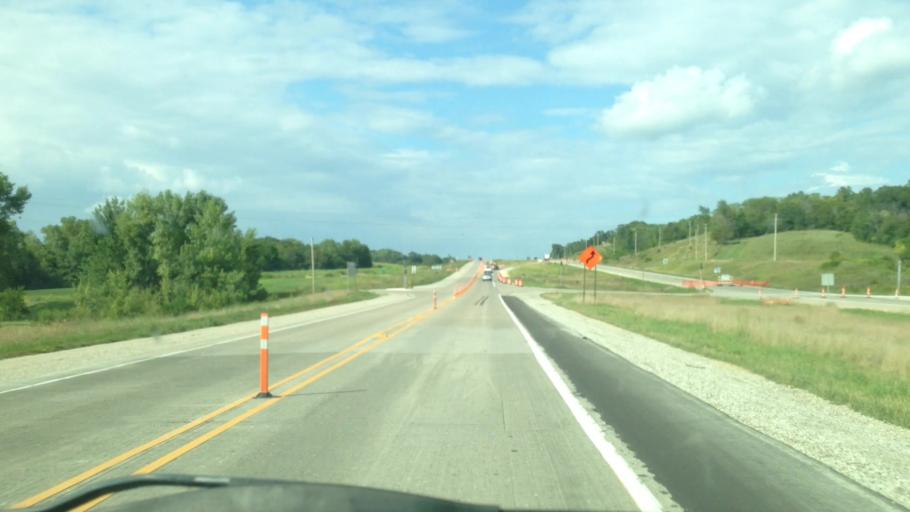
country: US
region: Iowa
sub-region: Henry County
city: Mount Pleasant
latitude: 40.9014
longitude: -91.5554
